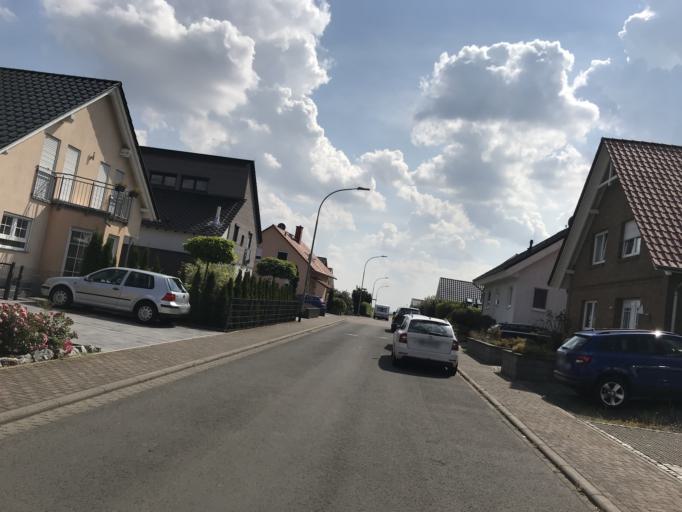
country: DE
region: Hesse
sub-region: Regierungsbezirk Darmstadt
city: Wolfersheim
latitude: 50.3914
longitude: 8.8027
